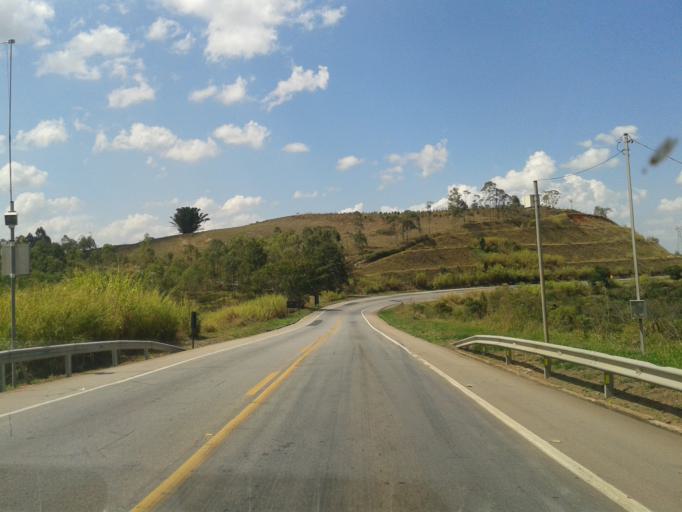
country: BR
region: Minas Gerais
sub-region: Campos Altos
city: Campos Altos
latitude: -19.7430
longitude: -45.9456
